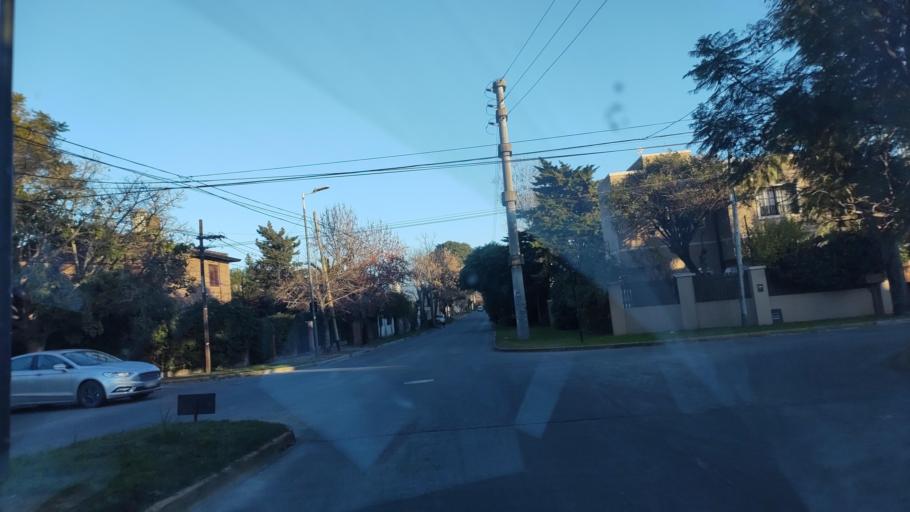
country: AR
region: Buenos Aires
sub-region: Partido de La Plata
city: La Plata
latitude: -34.8915
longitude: -58.0241
